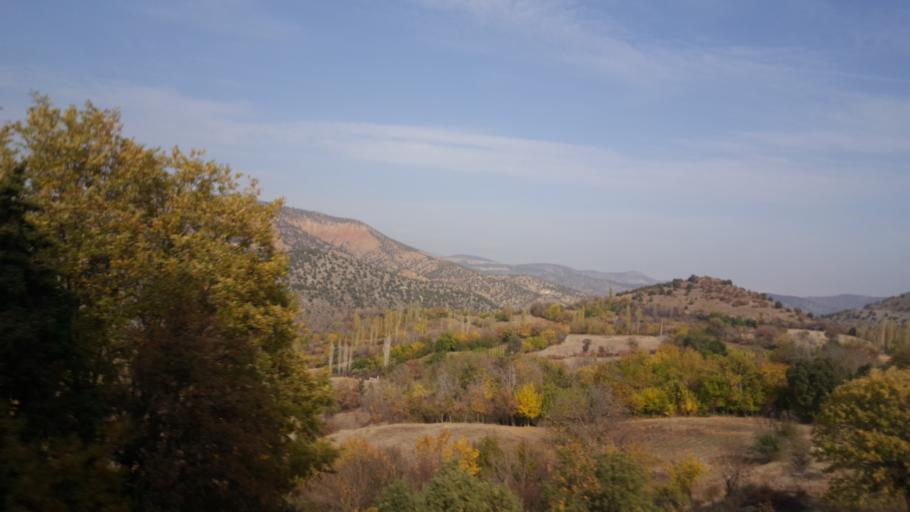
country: TR
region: Eskisehir
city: Mihaliccik
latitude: 39.9885
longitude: 31.3552
